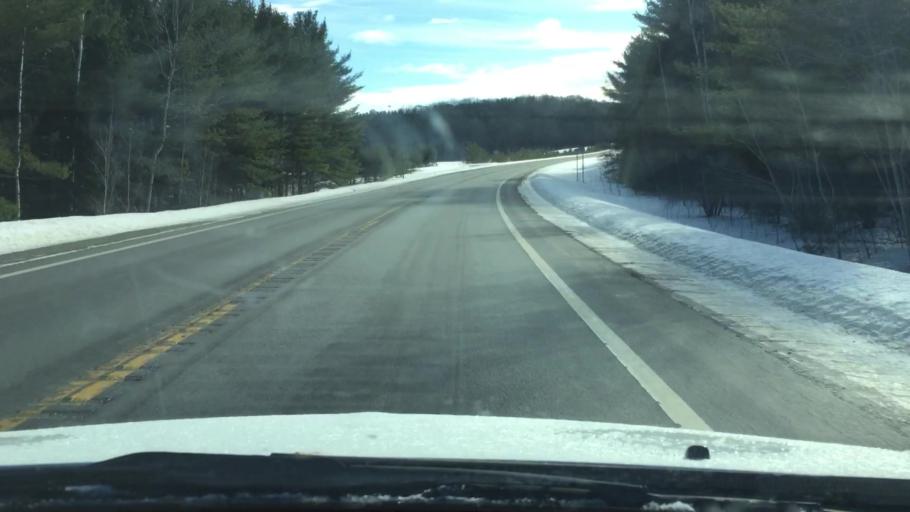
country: US
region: Michigan
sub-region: Antrim County
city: Mancelona
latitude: 44.9823
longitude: -85.0538
